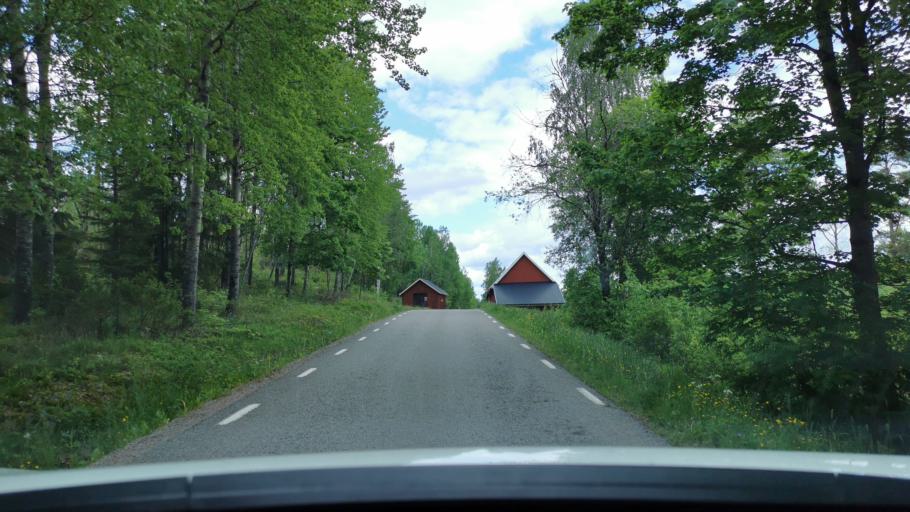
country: SE
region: Vaestra Goetaland
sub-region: Bengtsfors Kommun
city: Dals Langed
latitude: 58.8641
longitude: 12.3287
